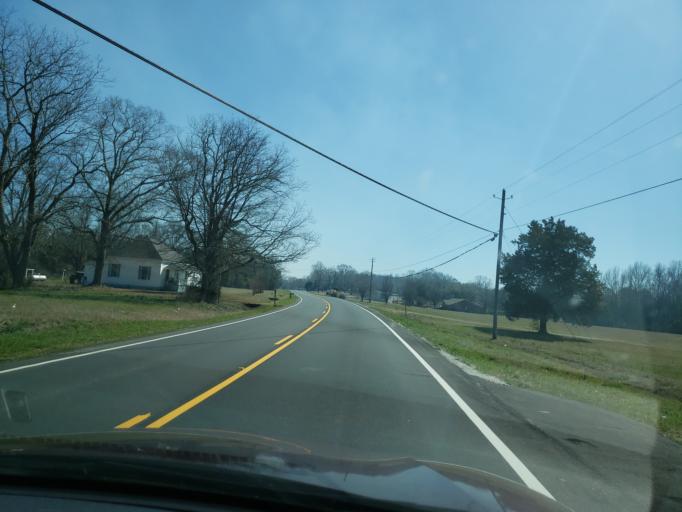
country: US
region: Alabama
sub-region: Macon County
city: Tuskegee
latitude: 32.5715
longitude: -85.6885
